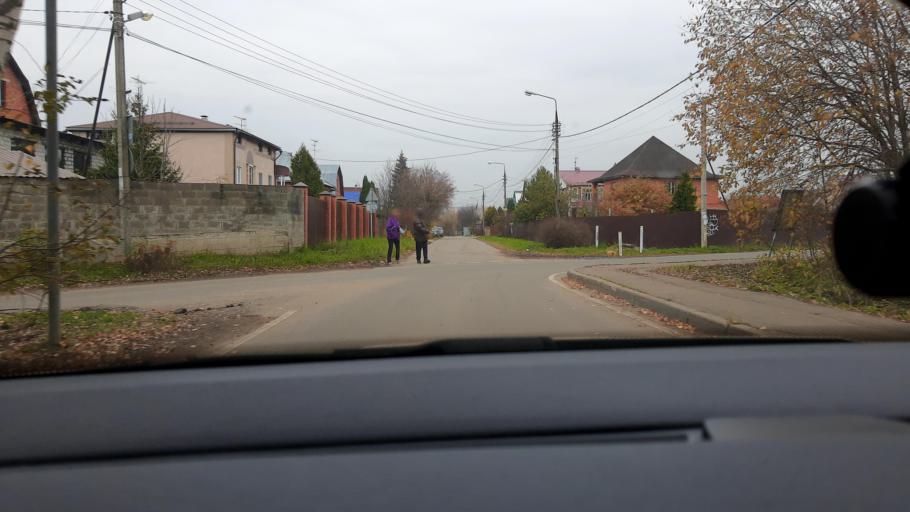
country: RU
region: Moskovskaya
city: Pirogovskiy
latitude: 55.9620
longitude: 37.7367
